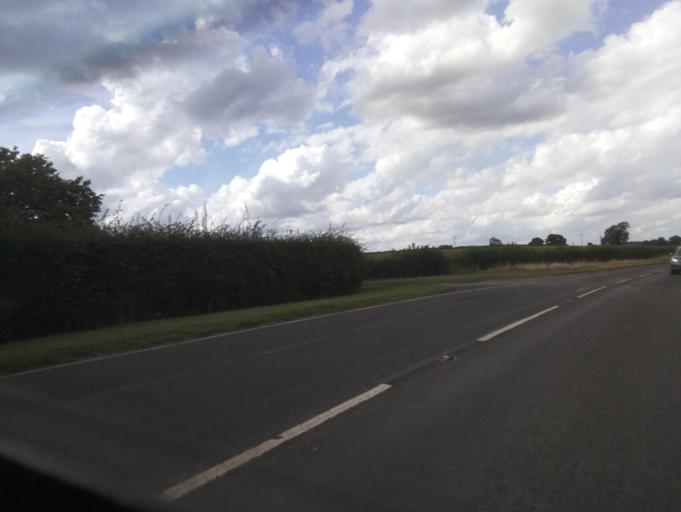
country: GB
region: England
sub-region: North Yorkshire
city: Ripon
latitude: 54.1655
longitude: -1.5490
